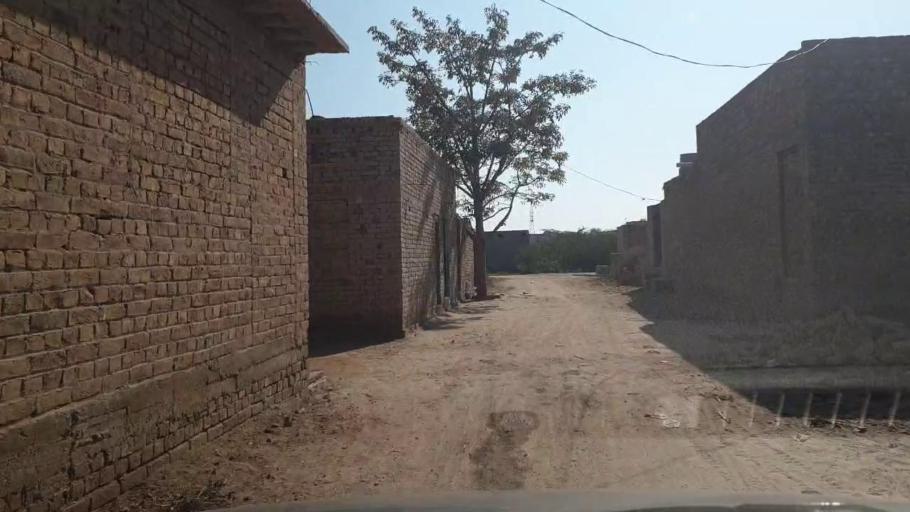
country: PK
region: Sindh
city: Shahpur Chakar
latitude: 26.1500
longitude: 68.6498
